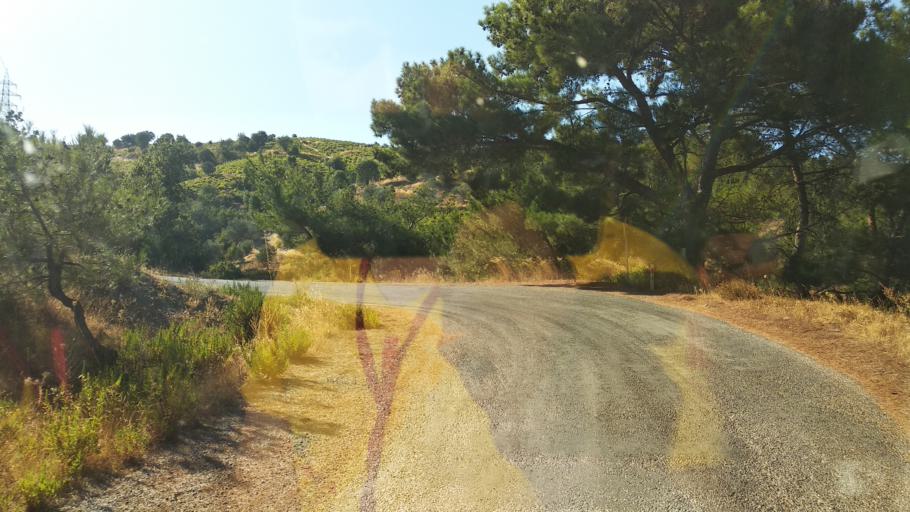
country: TR
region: Izmir
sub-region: Seferihisar
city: Seferhisar
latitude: 38.3274
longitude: 26.9548
